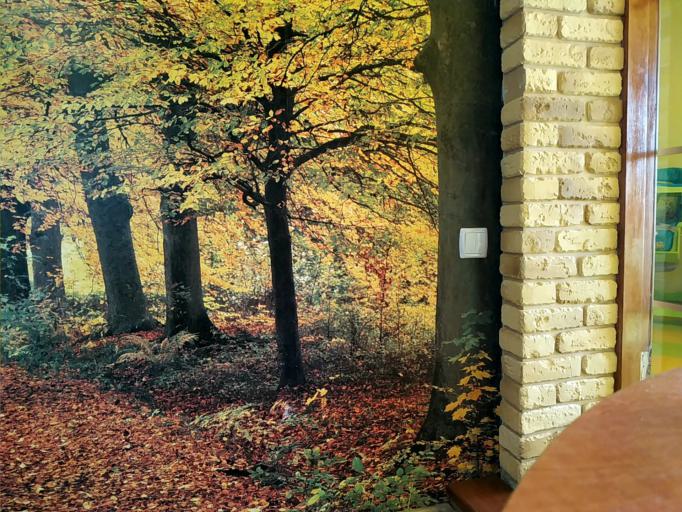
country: RU
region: Novgorod
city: Staraya Russa
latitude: 57.8333
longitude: 31.4820
